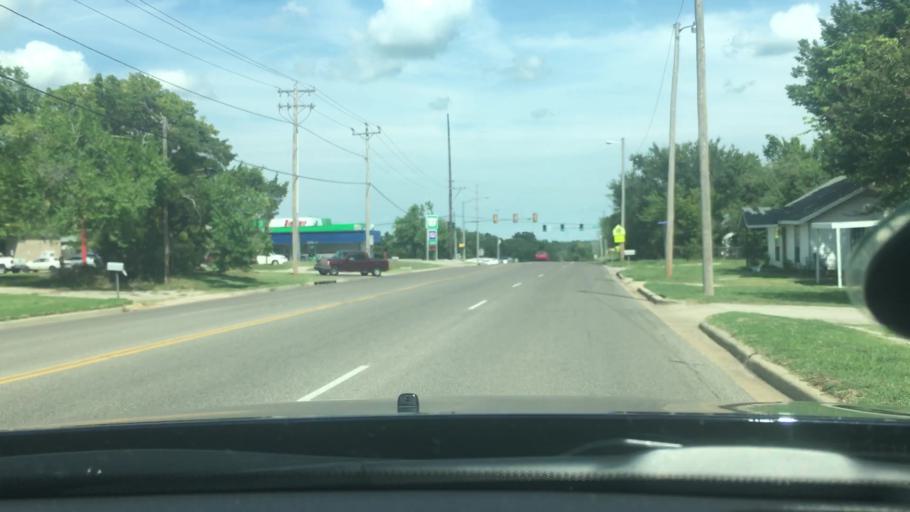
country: US
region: Oklahoma
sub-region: Pottawatomie County
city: Shawnee
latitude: 35.3326
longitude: -96.8961
